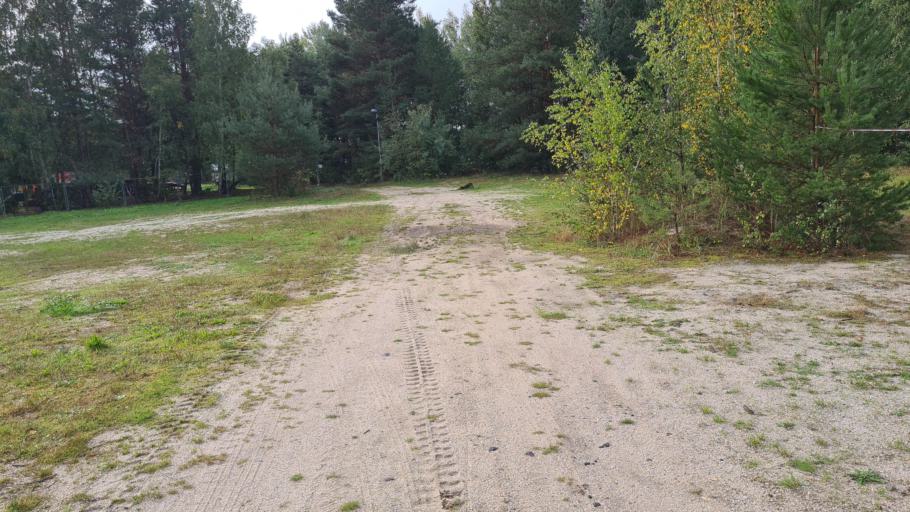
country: DE
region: Brandenburg
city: Sallgast
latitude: 51.5885
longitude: 13.7827
